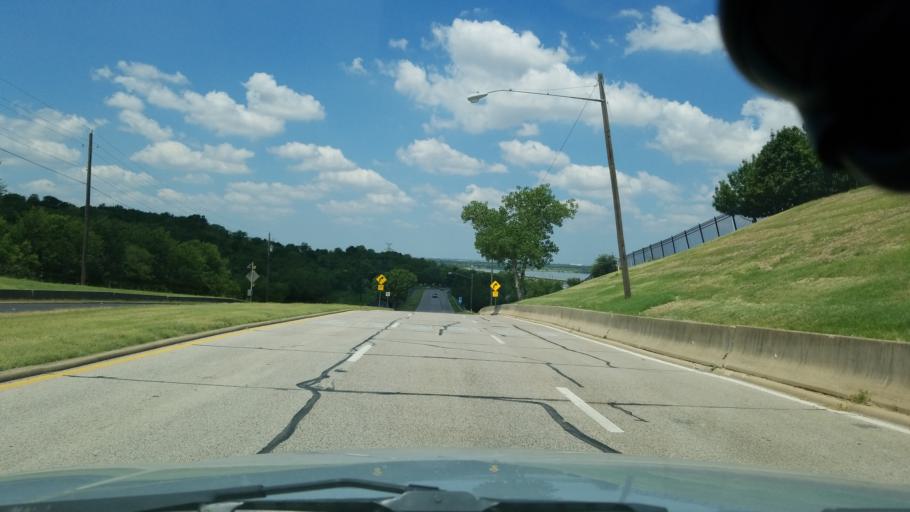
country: US
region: Texas
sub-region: Dallas County
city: Grand Prairie
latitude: 32.7058
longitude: -96.9463
